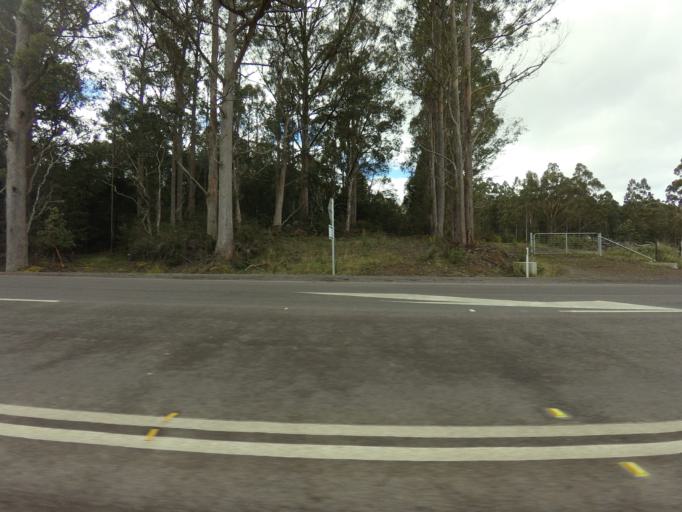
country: AU
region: Tasmania
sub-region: Huon Valley
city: Geeveston
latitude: -43.2533
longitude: 146.9970
